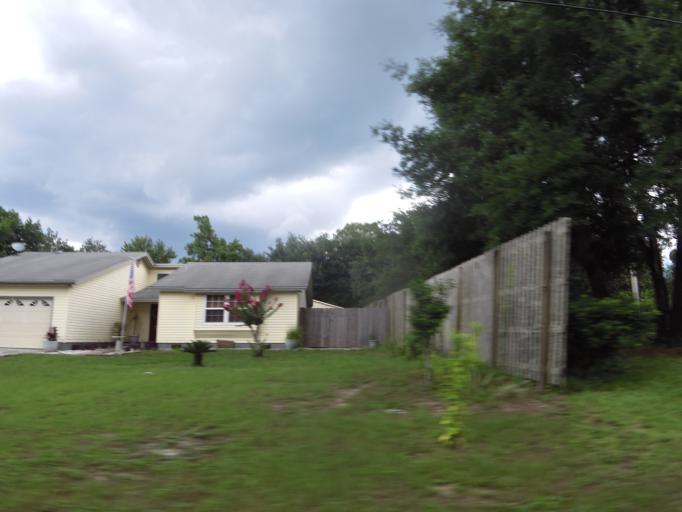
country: US
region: Florida
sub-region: Duval County
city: Atlantic Beach
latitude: 30.3564
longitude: -81.5120
